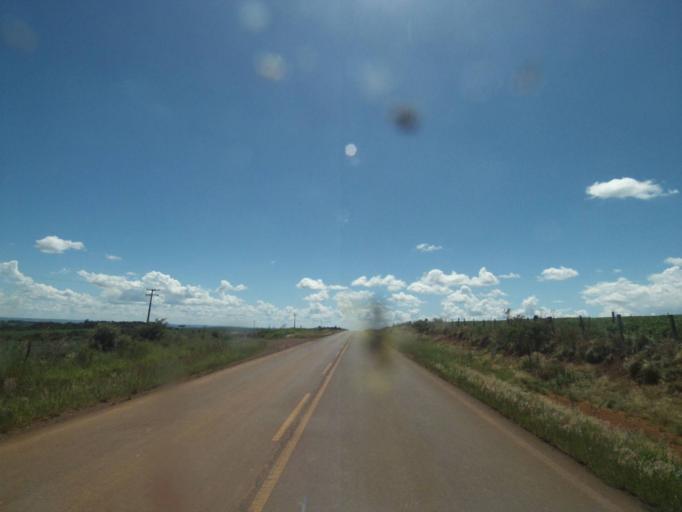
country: BR
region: Parana
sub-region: Pinhao
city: Pinhao
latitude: -25.8131
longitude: -52.0584
